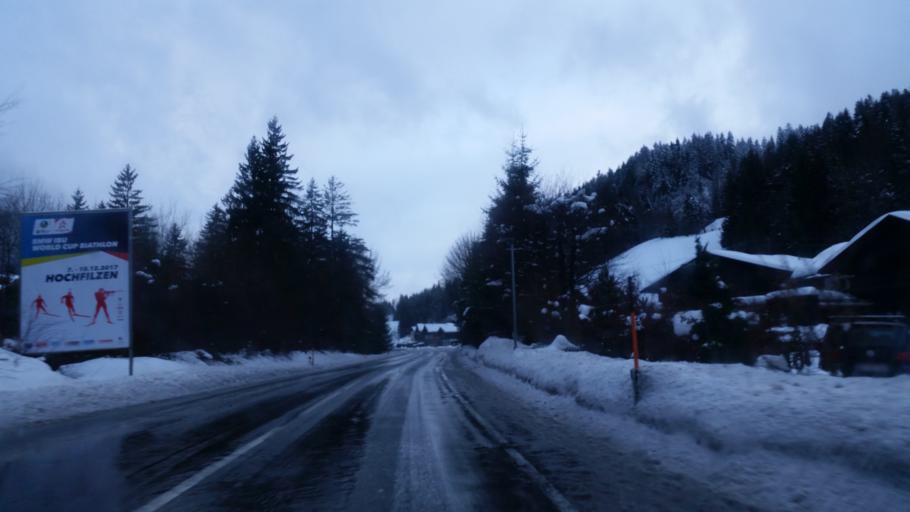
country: AT
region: Salzburg
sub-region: Politischer Bezirk Zell am See
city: Leogang
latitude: 47.4408
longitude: 12.7167
